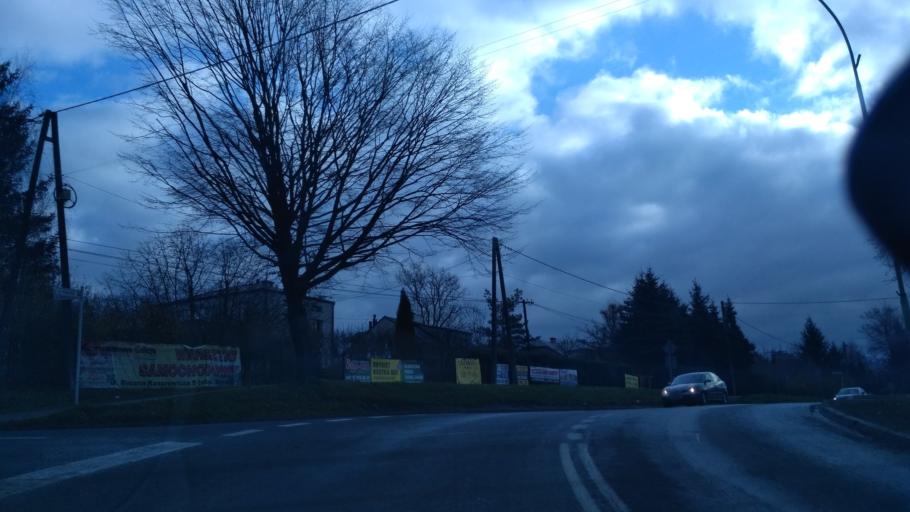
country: PL
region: Subcarpathian Voivodeship
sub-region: Powiat lancucki
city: Lancut
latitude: 50.0766
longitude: 22.2361
